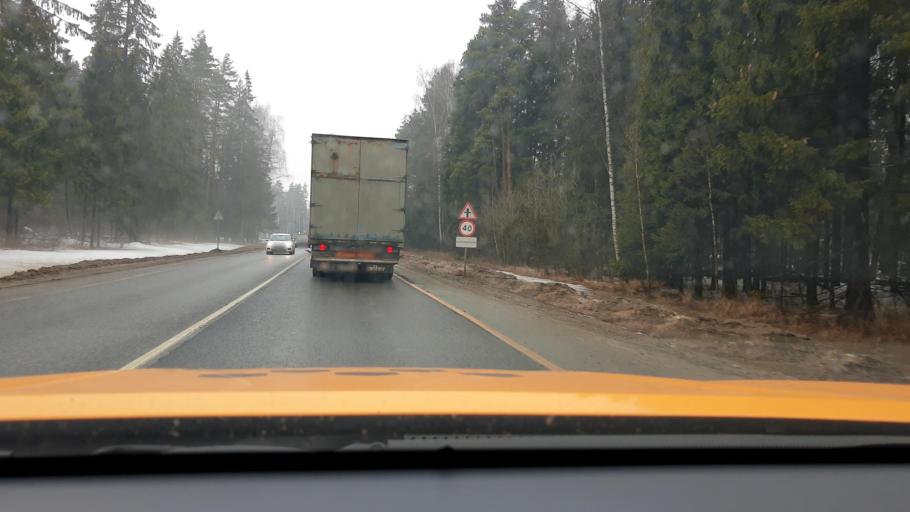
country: RU
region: Moskovskaya
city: Chernogolovka
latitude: 55.9832
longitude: 38.3424
